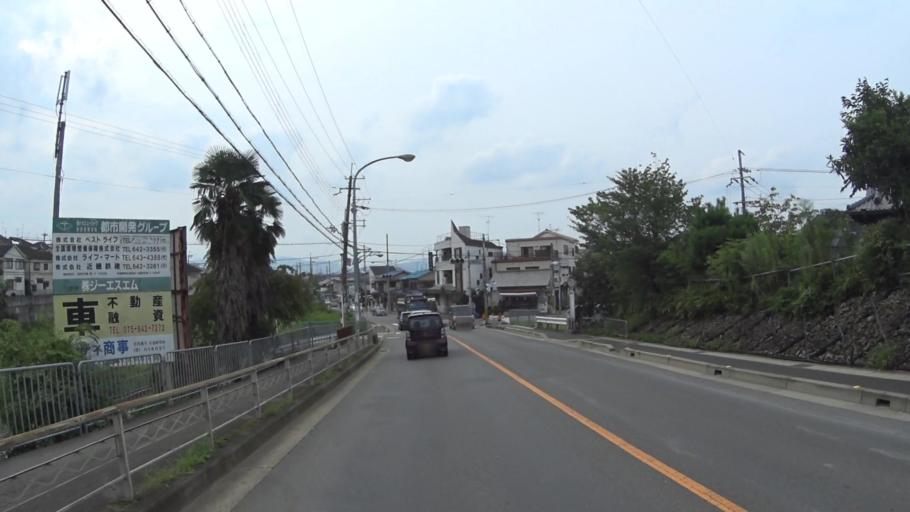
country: JP
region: Kyoto
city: Uji
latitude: 34.9542
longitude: 135.7807
